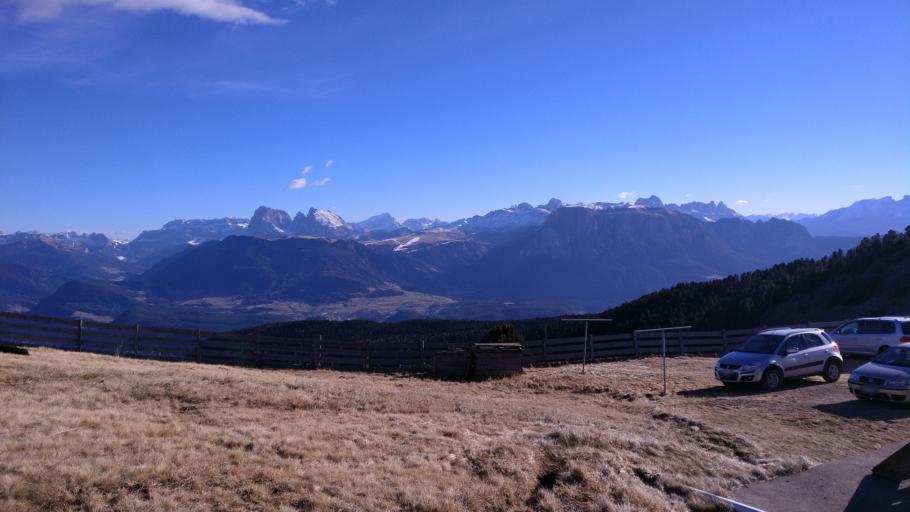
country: IT
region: Trentino-Alto Adige
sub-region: Bolzano
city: Renon - Ritten
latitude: 46.6040
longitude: 11.4583
